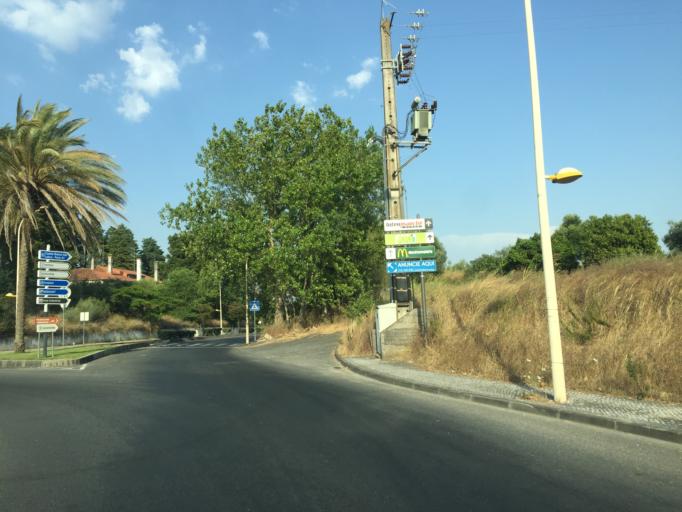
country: PT
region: Santarem
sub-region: Torres Novas
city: Torres Novas
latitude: 39.4750
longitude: -8.5598
